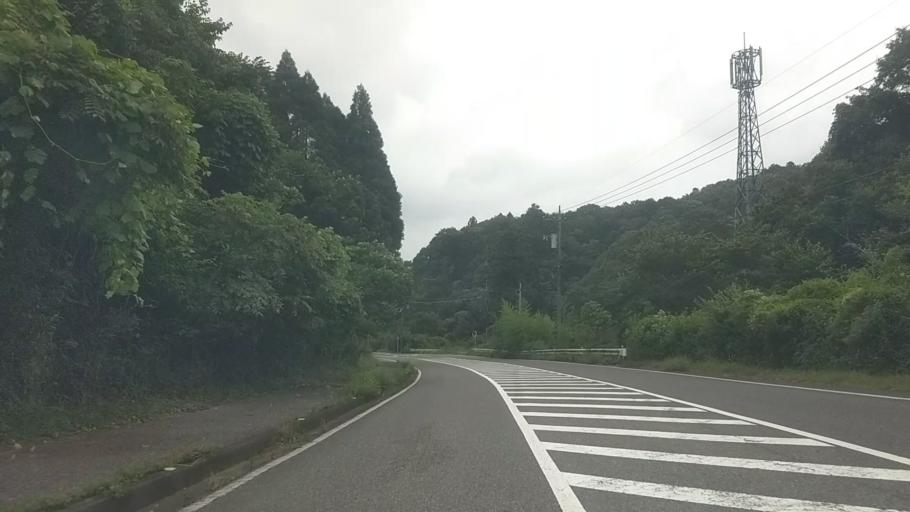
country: JP
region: Chiba
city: Kawaguchi
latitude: 35.2399
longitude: 140.0350
